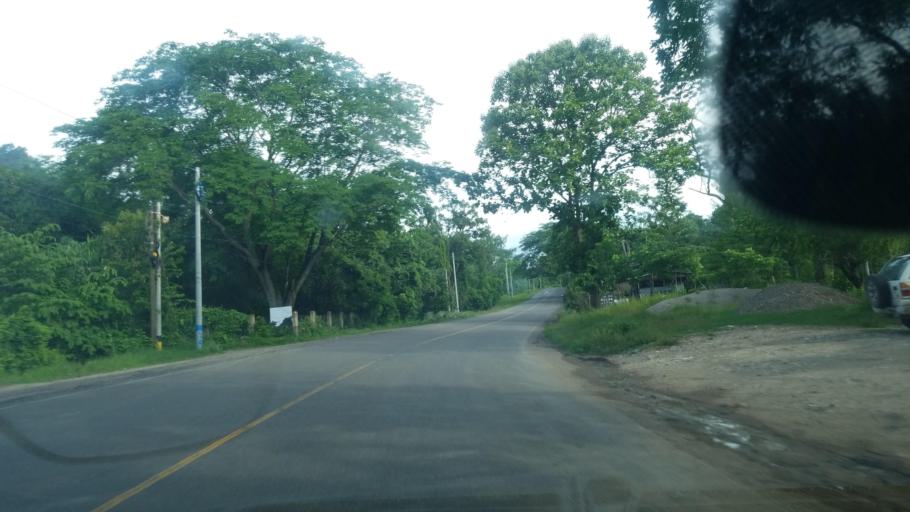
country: HN
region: Santa Barbara
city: Trinidad
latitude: 15.1200
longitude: -88.2009
